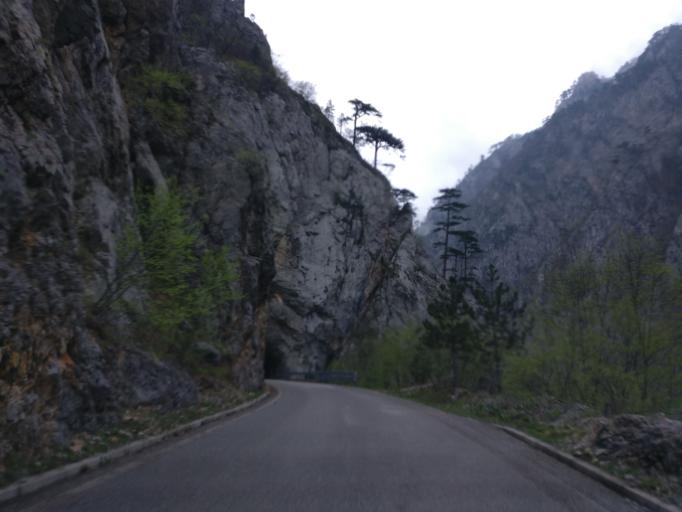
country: ME
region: Opstina Pluzine
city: Pluzine
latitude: 43.2806
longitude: 18.8494
